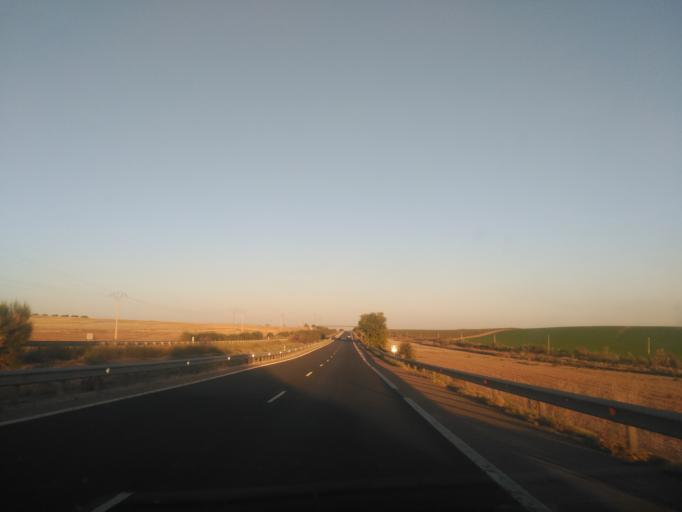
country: ES
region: Castille and Leon
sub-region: Provincia de Valladolid
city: Cisterniga
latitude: 41.5970
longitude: -4.6441
